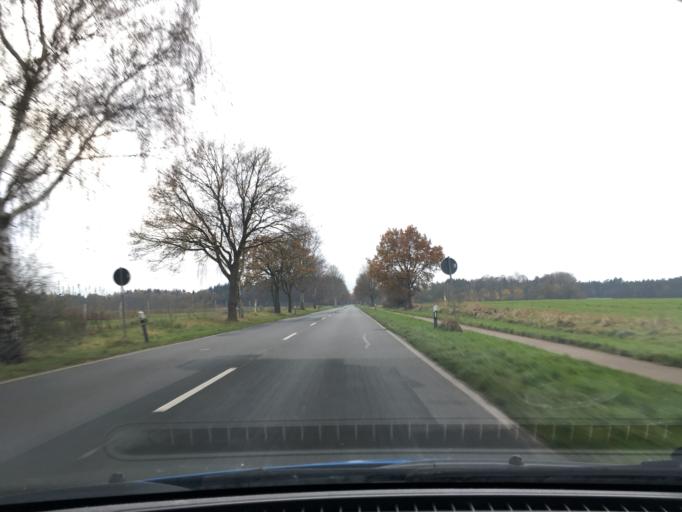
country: DE
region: Lower Saxony
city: Embsen
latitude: 53.2079
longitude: 10.3658
